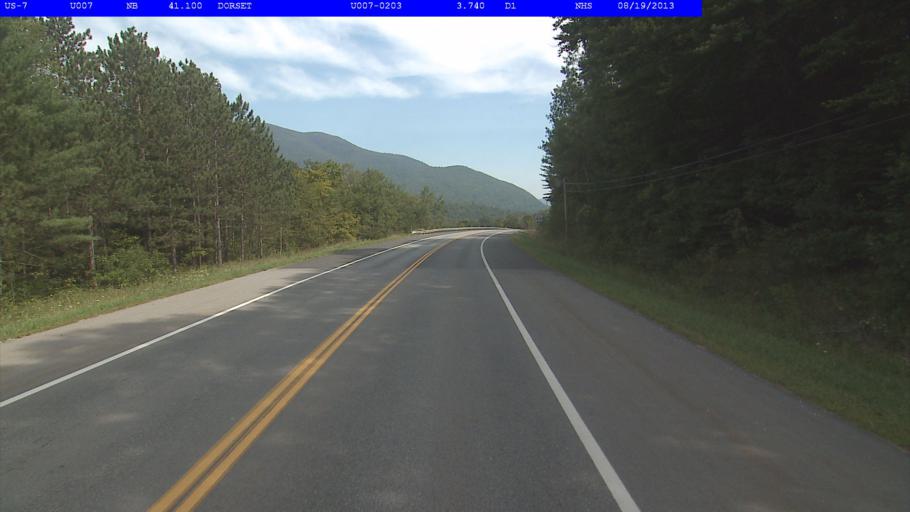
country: US
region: Vermont
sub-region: Bennington County
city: Manchester Center
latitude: 43.2632
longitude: -73.0079
